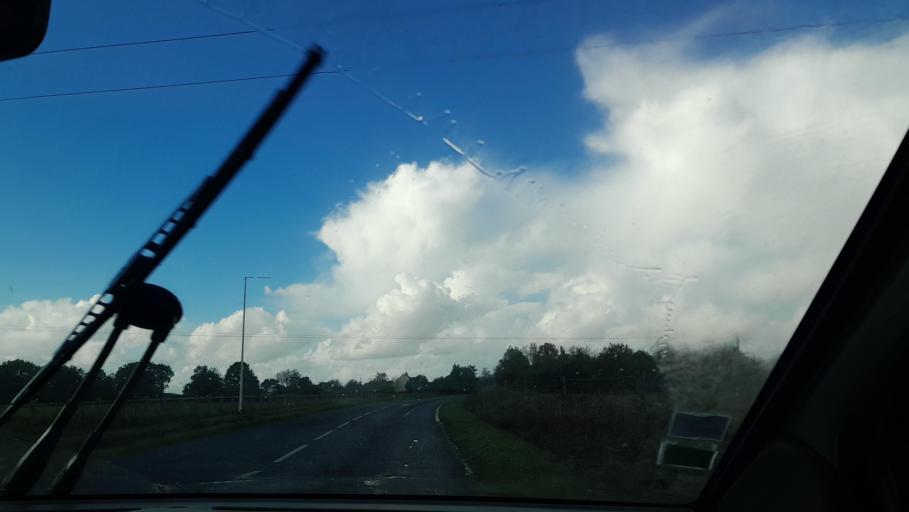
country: FR
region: Pays de la Loire
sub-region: Departement de la Mayenne
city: Cosse-le-Vivien
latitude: 47.9384
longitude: -0.9012
